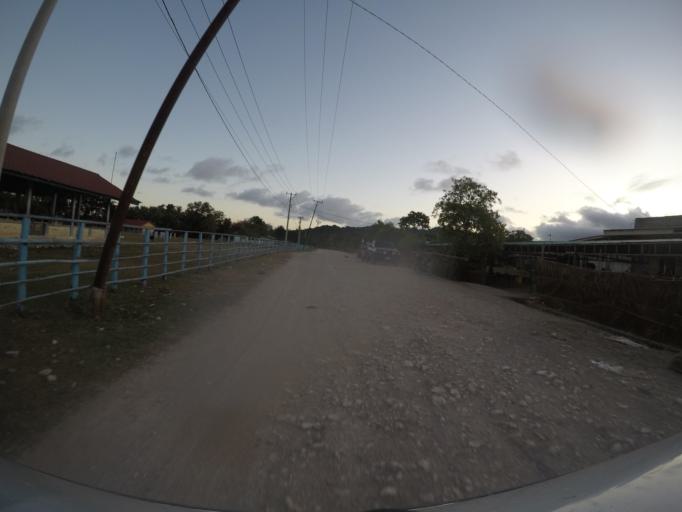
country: TL
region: Viqueque
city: Viqueque
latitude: -8.7738
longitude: 126.6386
